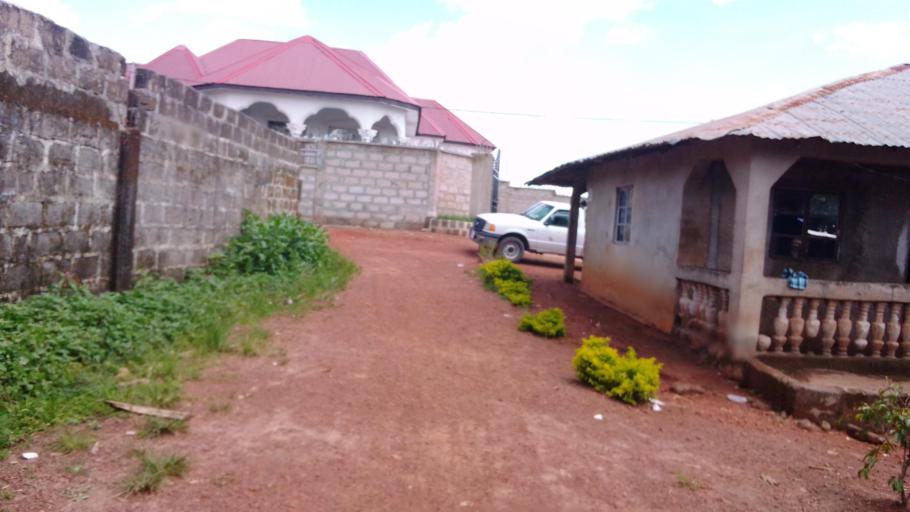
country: SL
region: Northern Province
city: Makeni
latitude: 8.8808
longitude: -12.0276
